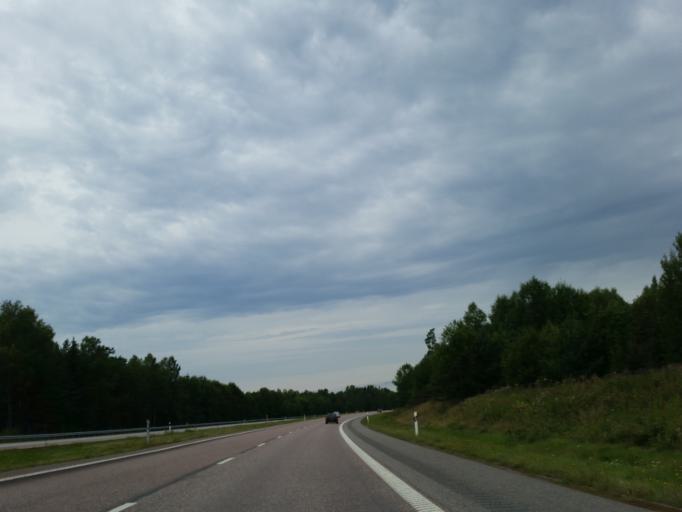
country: SE
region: Stockholm
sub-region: Nykvarns Kommun
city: Nykvarn
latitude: 59.2013
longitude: 17.3724
